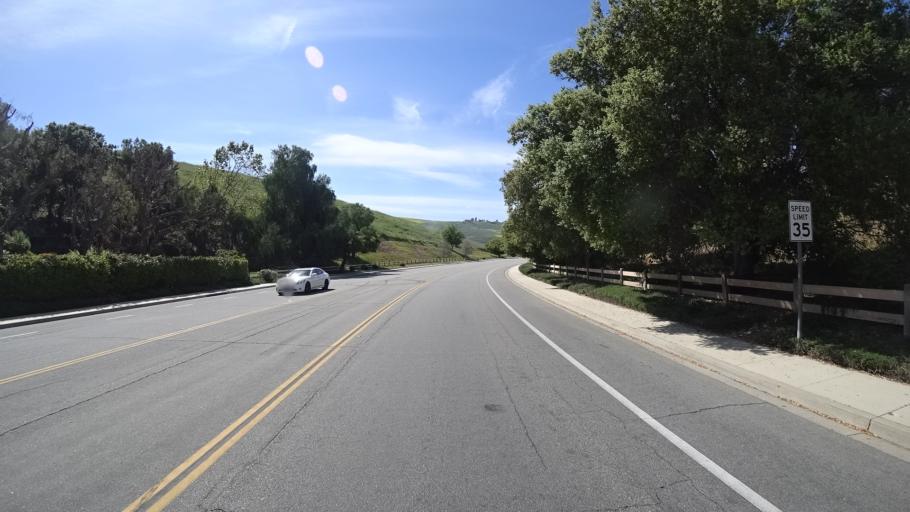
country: US
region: California
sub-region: Ventura County
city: Thousand Oaks
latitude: 34.2150
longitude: -118.8355
